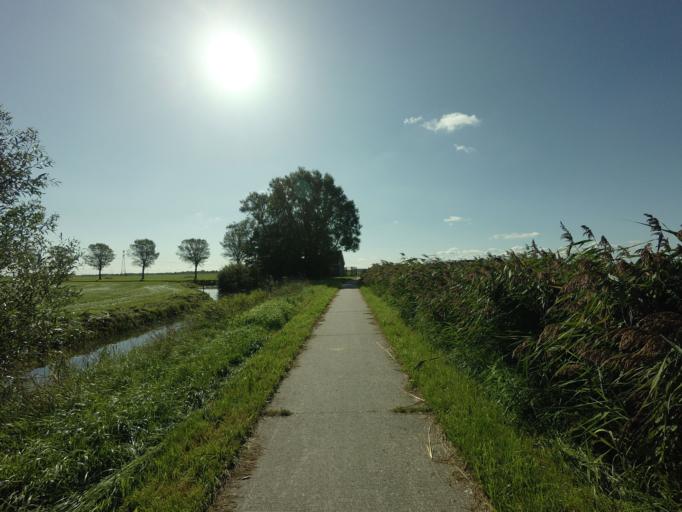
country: NL
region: Friesland
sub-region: Gemeente Boarnsterhim
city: Reduzum
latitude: 53.1210
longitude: 5.7563
